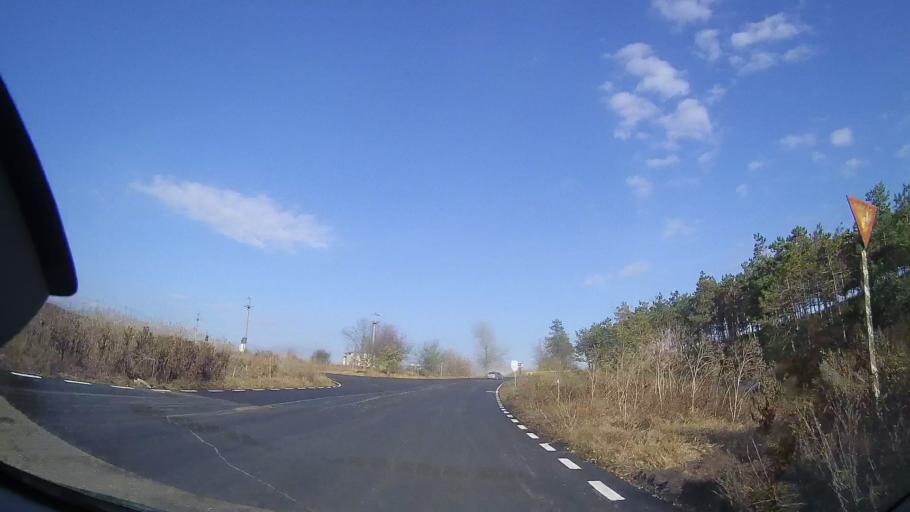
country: RO
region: Constanta
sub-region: Comuna Limanu
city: Limanu
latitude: 43.8225
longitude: 28.5227
